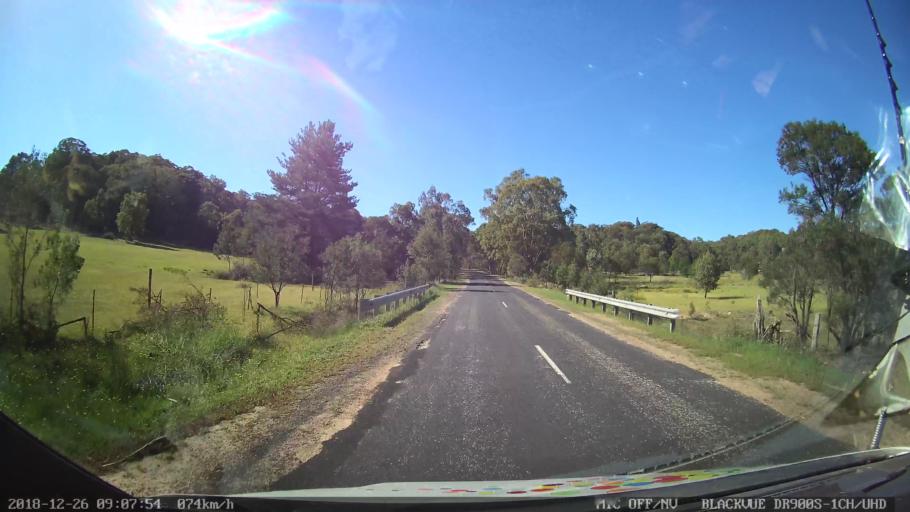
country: AU
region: New South Wales
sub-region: Mid-Western Regional
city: Kandos
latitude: -32.7106
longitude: 150.0030
